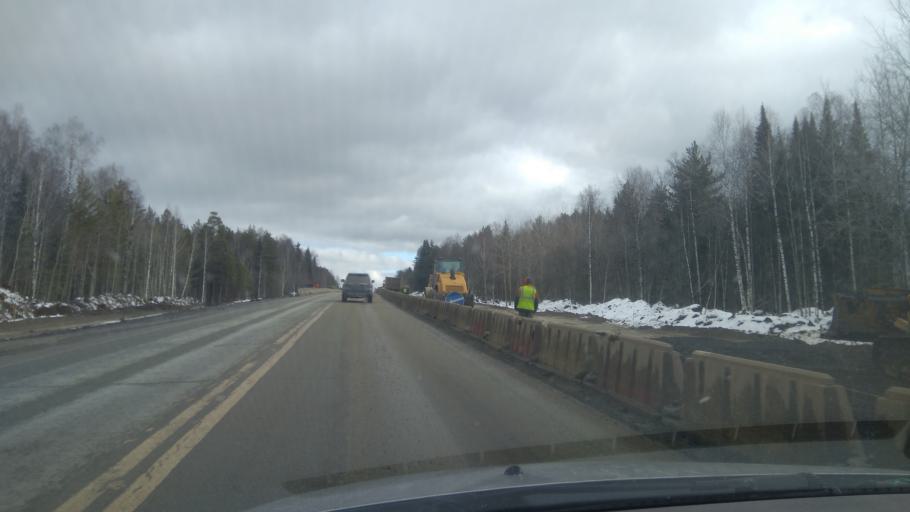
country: RU
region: Sverdlovsk
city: Bisert'
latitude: 56.8340
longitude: 58.9367
